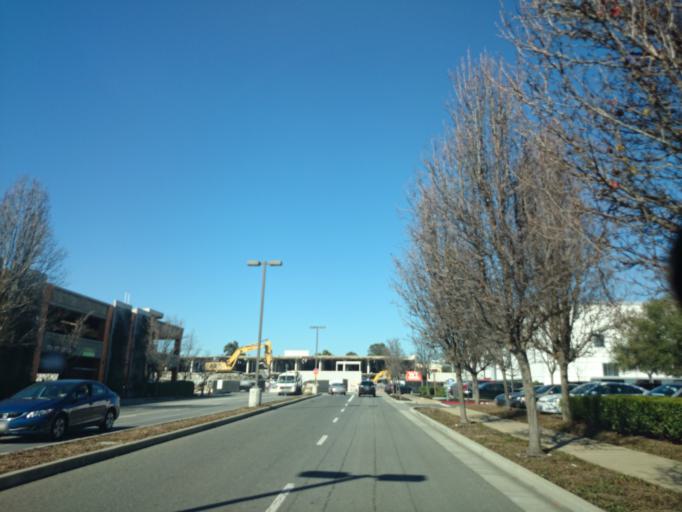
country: US
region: California
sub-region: San Mateo County
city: Menlo Park
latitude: 37.4427
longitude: -122.1690
